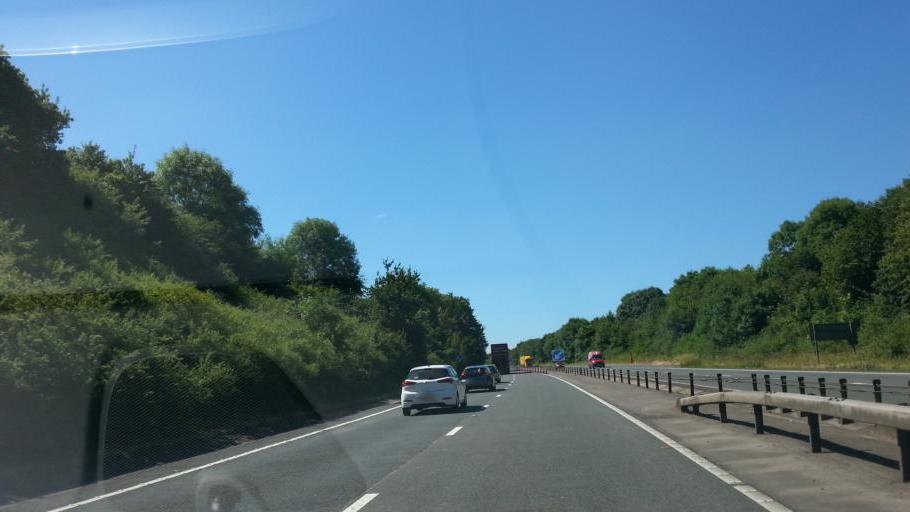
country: GB
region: Wales
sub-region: Monmouthshire
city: Llanbadoc
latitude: 51.6976
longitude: -2.8782
